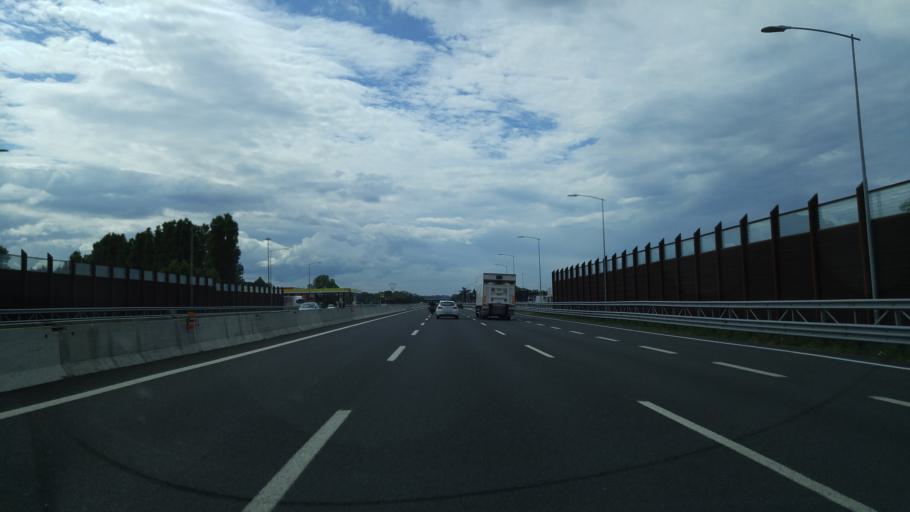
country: IT
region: Emilia-Romagna
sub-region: Provincia di Rimini
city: Coriano
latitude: 43.9931
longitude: 12.6224
